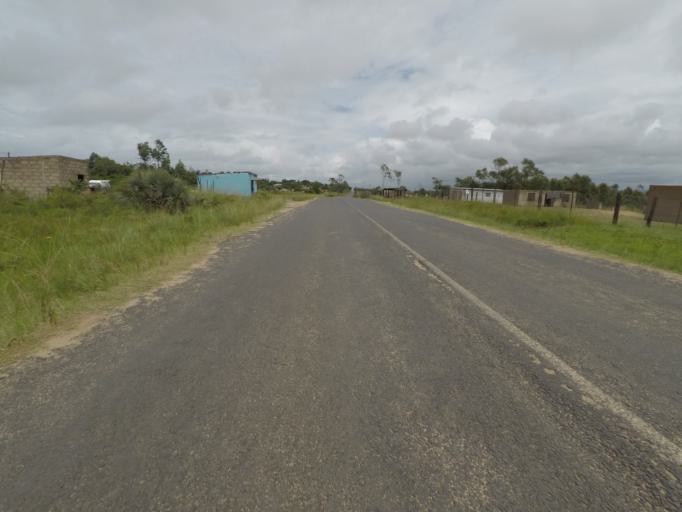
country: ZA
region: KwaZulu-Natal
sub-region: uThungulu District Municipality
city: eSikhawini
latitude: -28.9147
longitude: 31.8489
